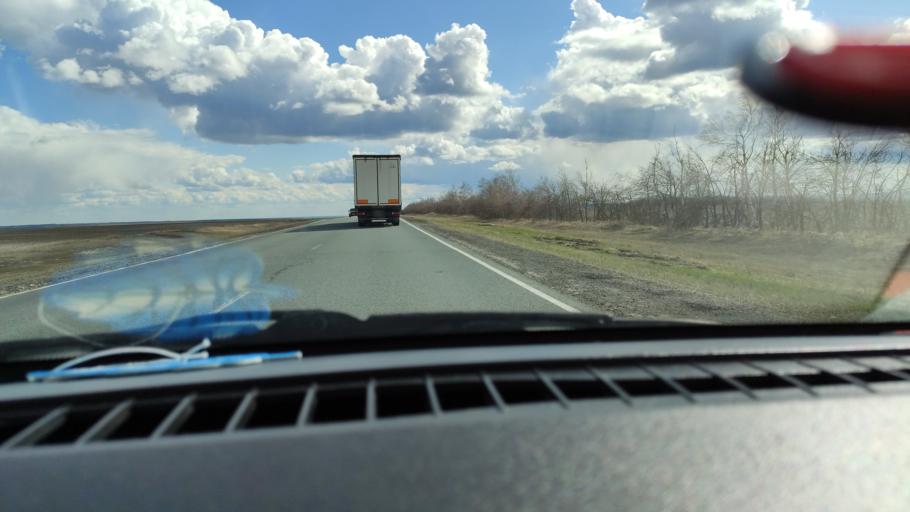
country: RU
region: Saratov
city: Dukhovnitskoye
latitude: 52.7889
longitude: 48.2326
